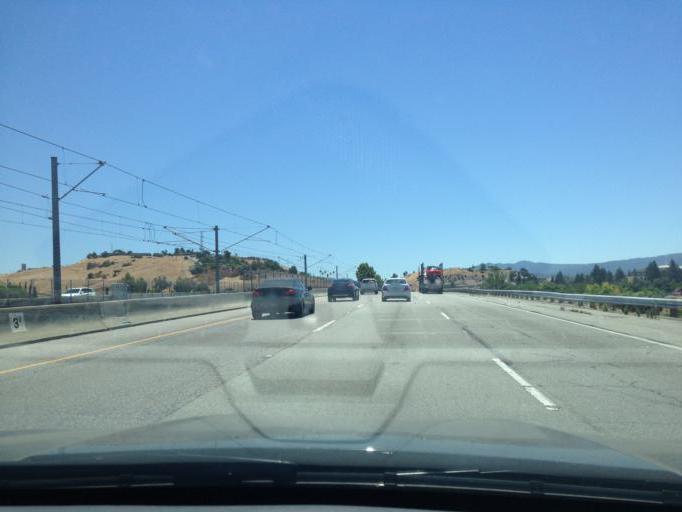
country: US
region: California
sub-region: Santa Clara County
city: Seven Trees
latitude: 37.2963
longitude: -121.8739
